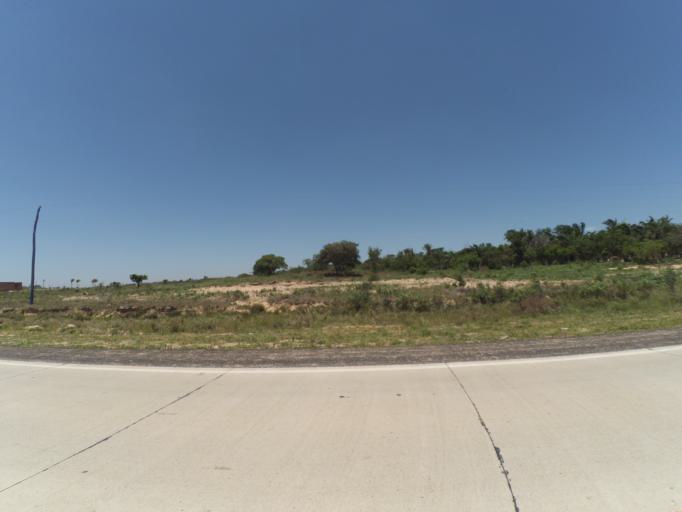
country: BO
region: Santa Cruz
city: Santa Cruz de la Sierra
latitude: -17.8056
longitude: -63.2800
